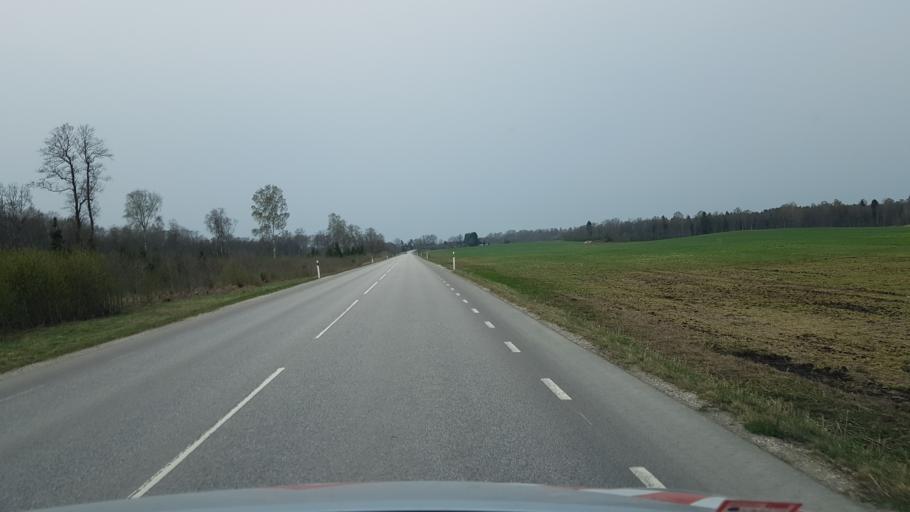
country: EE
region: Harju
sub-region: Raasiku vald
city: Arukula
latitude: 59.3738
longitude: 25.0225
